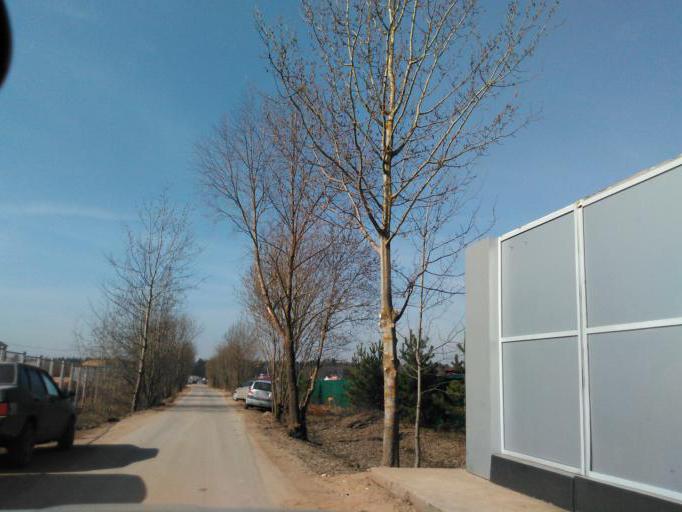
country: RU
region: Moskovskaya
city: Opalikha
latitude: 55.8756
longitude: 37.2579
